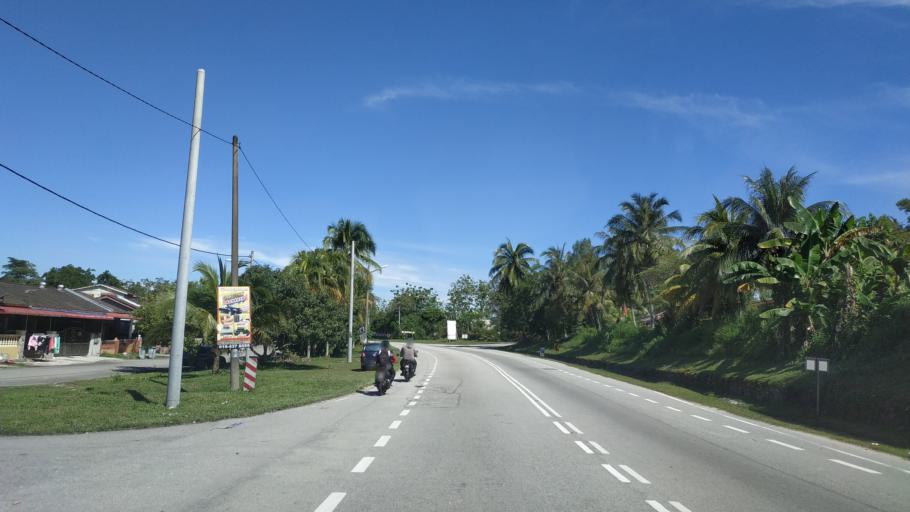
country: MY
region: Kedah
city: Kulim
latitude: 5.3472
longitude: 100.5374
